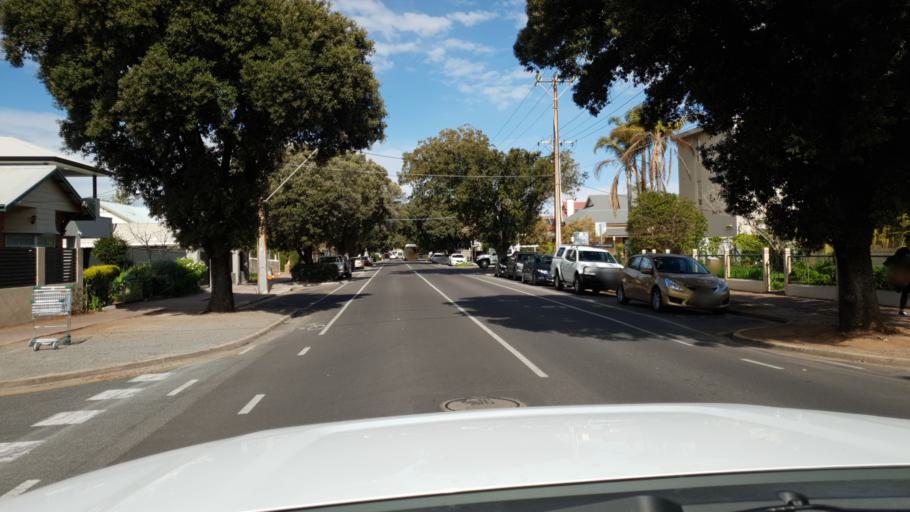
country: AU
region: South Australia
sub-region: Adelaide
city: Glenelg
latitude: -34.9830
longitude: 138.5133
